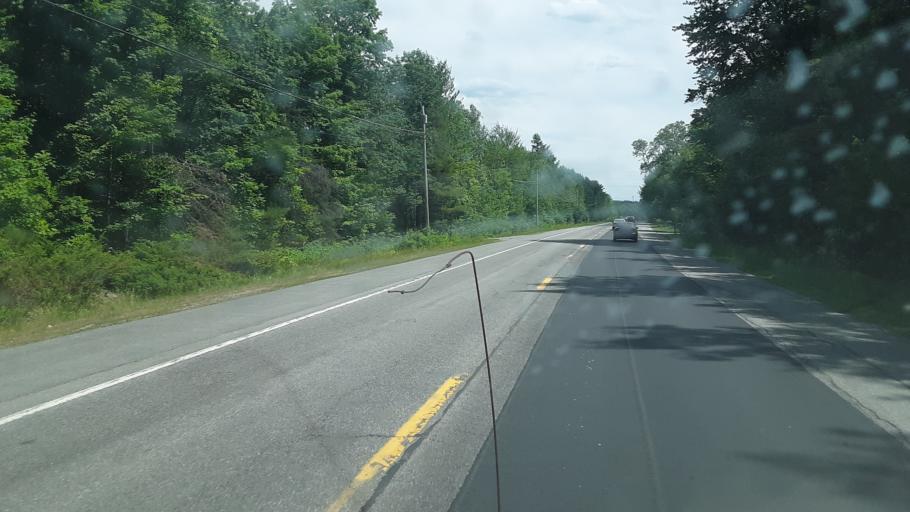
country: US
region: Maine
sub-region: Kennebec County
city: Oakland
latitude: 44.6468
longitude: -69.6939
